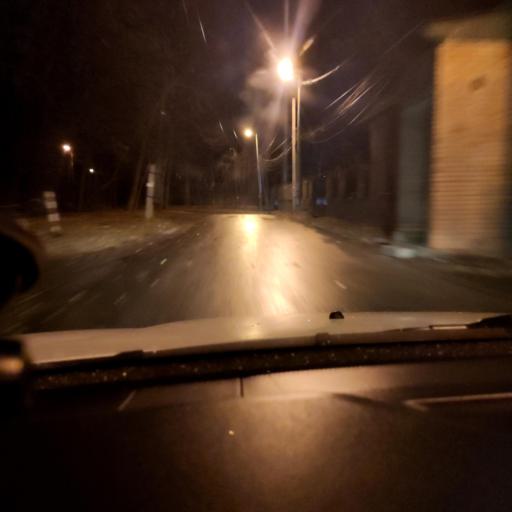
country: RU
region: Samara
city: Samara
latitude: 53.2895
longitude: 50.1975
